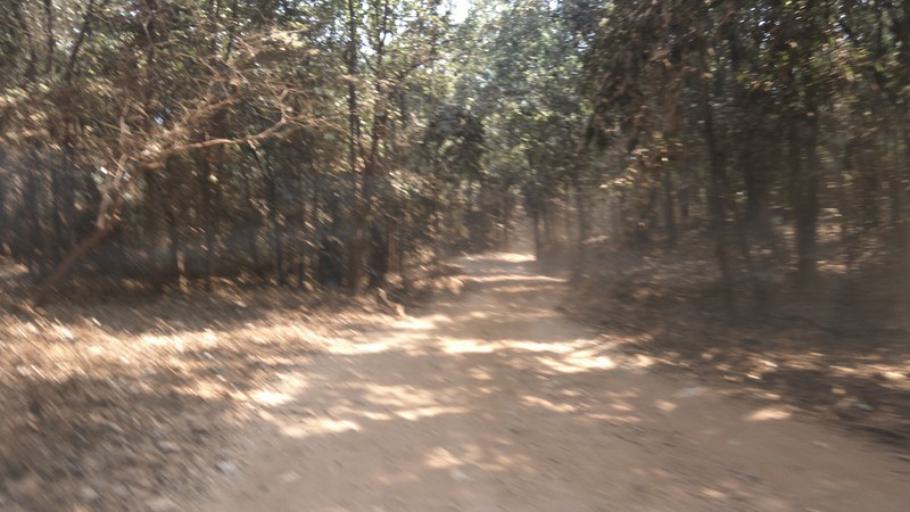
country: IN
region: Goa
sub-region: South Goa
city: Sanguem
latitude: 15.3261
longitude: 74.2832
